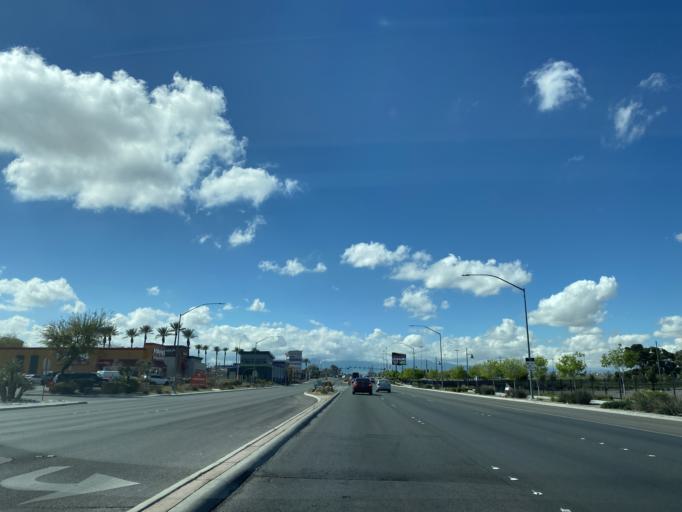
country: US
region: Nevada
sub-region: Clark County
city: North Las Vegas
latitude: 36.2395
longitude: -115.1488
